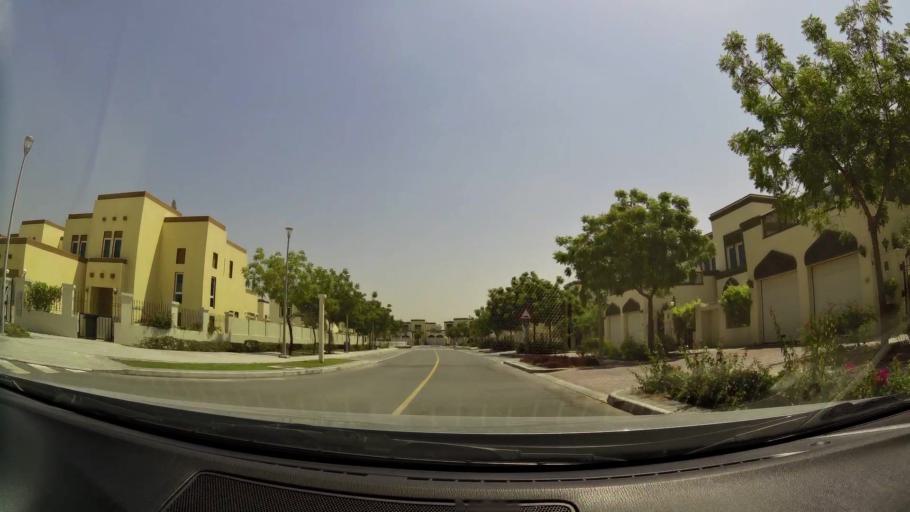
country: AE
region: Dubai
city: Dubai
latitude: 25.0405
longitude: 55.1680
